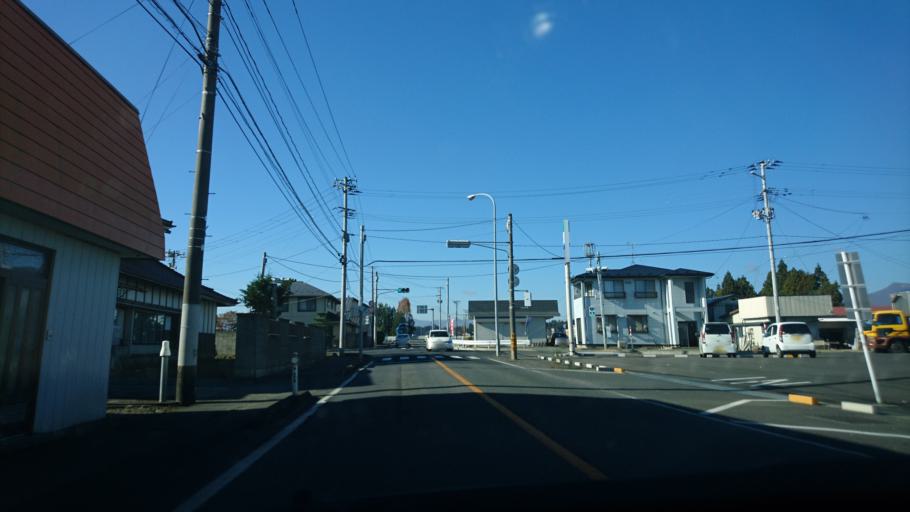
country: JP
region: Iwate
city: Mizusawa
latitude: 39.1296
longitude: 141.0537
